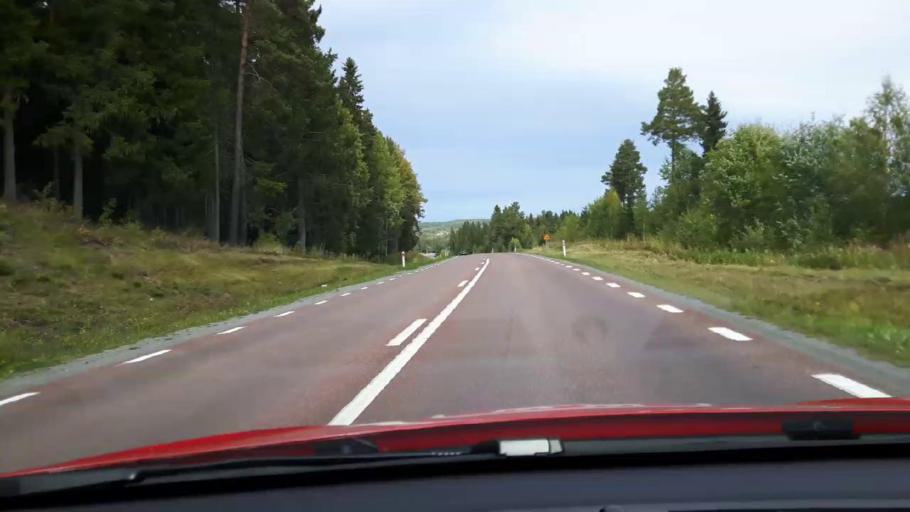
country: SE
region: Jaemtland
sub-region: OEstersunds Kommun
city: Brunflo
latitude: 63.0575
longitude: 14.8330
